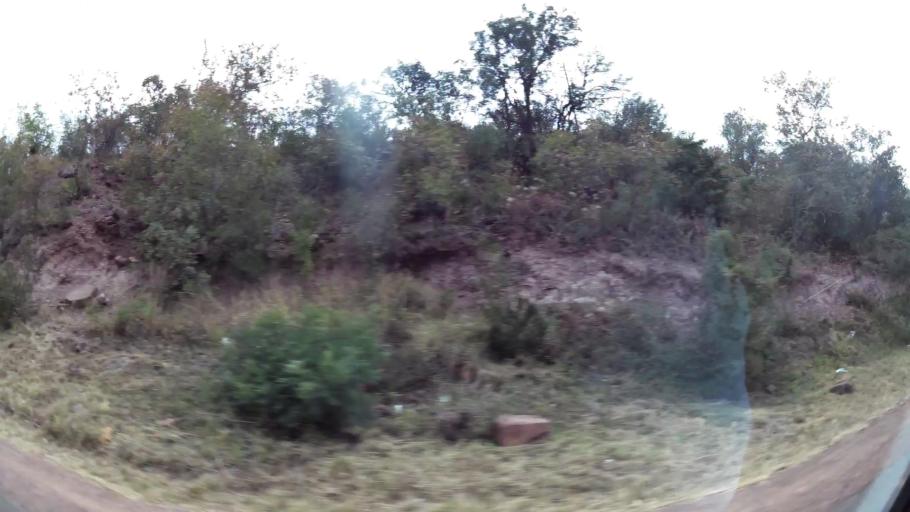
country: ZA
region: Limpopo
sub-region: Waterberg District Municipality
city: Modimolle
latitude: -24.6681
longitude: 28.4552
